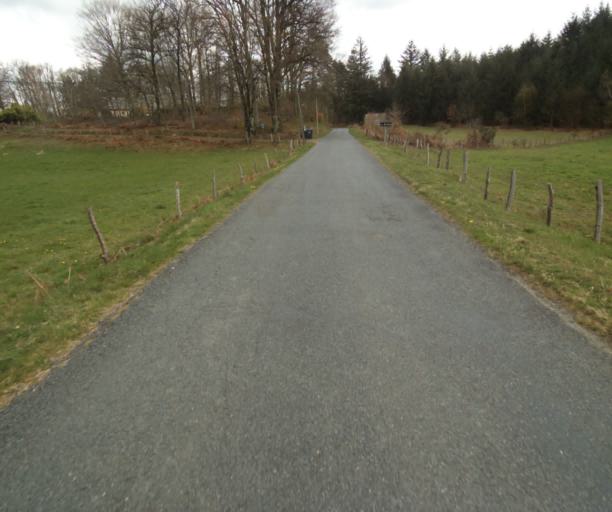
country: FR
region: Limousin
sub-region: Departement de la Correze
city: Correze
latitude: 45.3641
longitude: 1.9277
